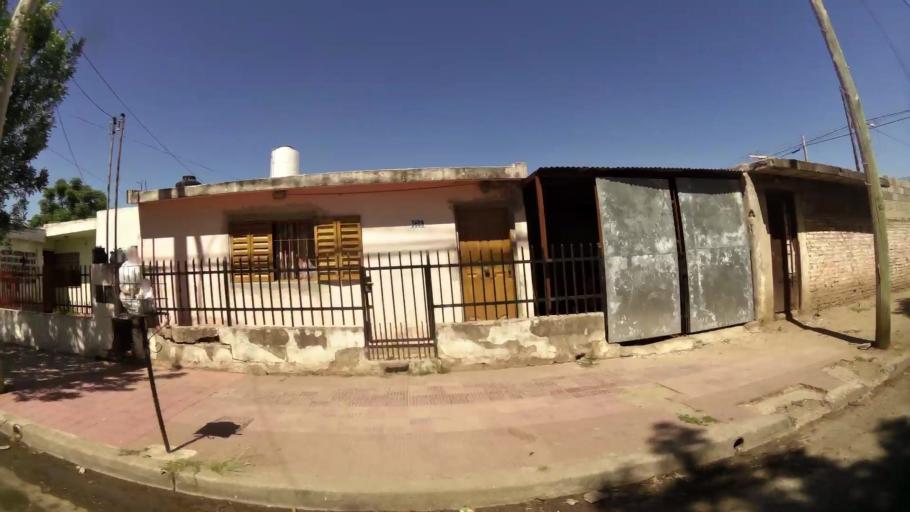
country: AR
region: Cordoba
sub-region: Departamento de Capital
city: Cordoba
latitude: -31.3687
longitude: -64.1429
